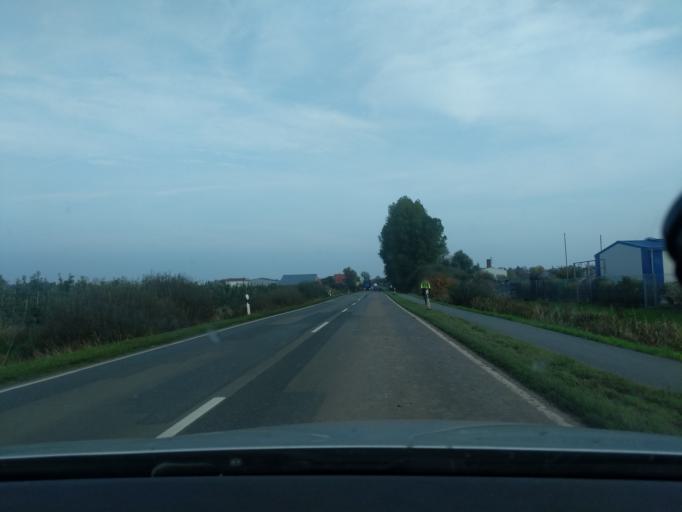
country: DE
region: Lower Saxony
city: Guderhandviertel
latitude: 53.5443
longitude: 9.6028
